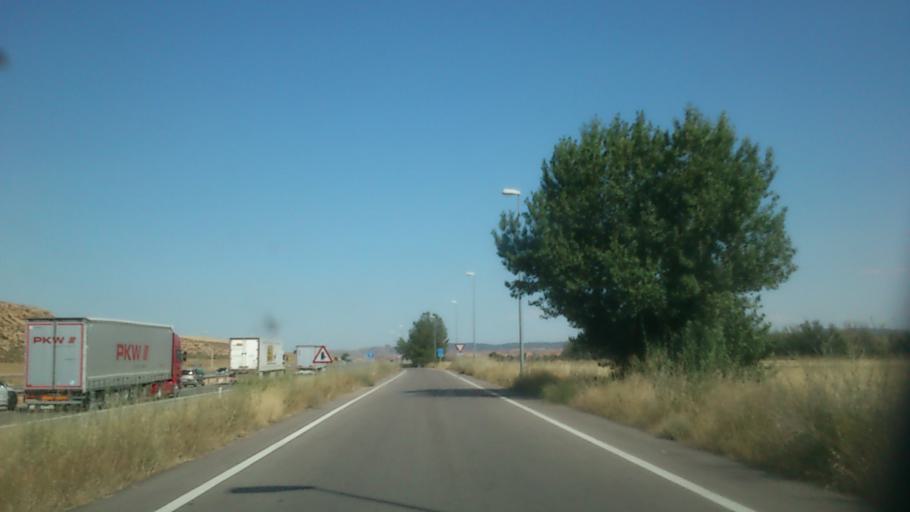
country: ES
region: Aragon
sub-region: Provincia de Zaragoza
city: Cetina
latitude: 41.3110
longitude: -1.9996
